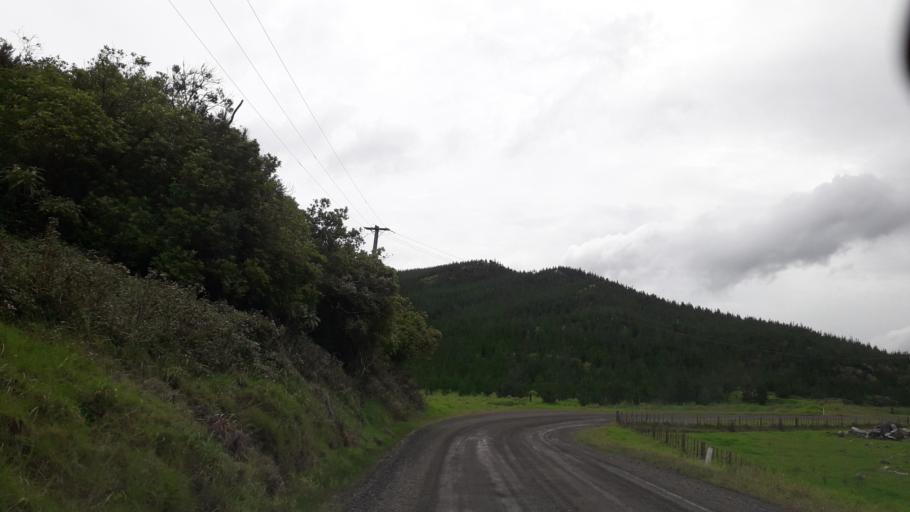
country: NZ
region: Northland
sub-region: Far North District
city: Ahipara
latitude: -35.4319
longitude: 173.3473
